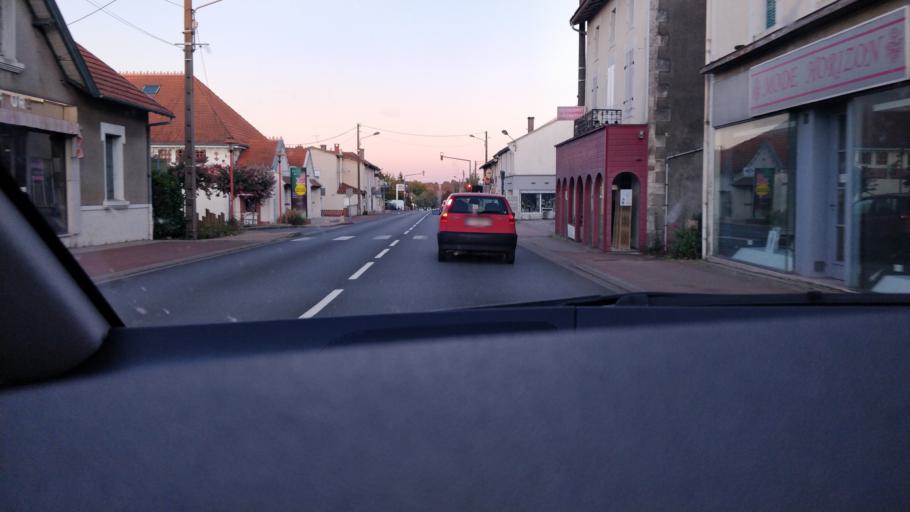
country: FR
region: Poitou-Charentes
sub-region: Departement de la Charente
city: Loubert
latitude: 45.8861
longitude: 0.5818
